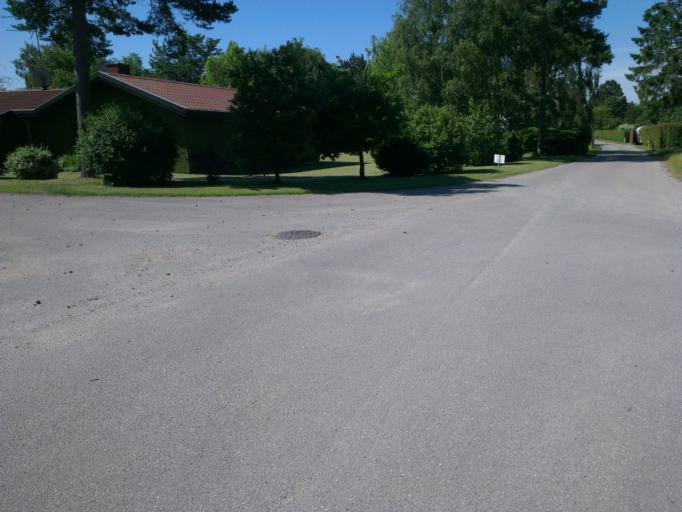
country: DK
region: Capital Region
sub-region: Frederikssund Kommune
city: Jaegerspris
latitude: 55.8175
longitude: 11.9435
